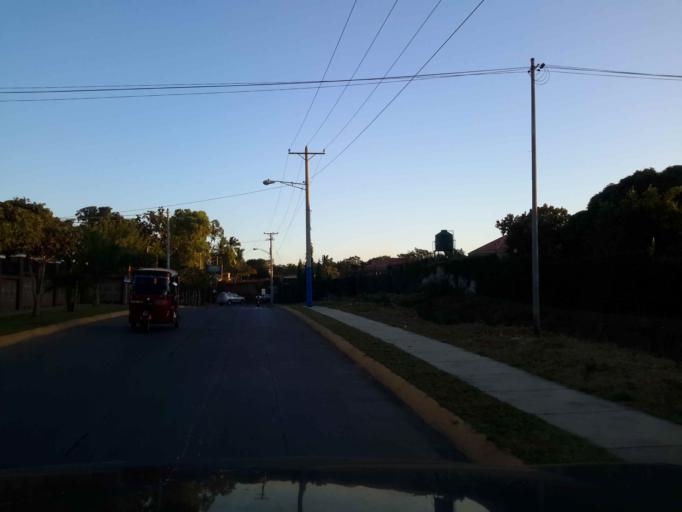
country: NI
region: Managua
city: Managua
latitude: 12.1016
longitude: -86.2377
